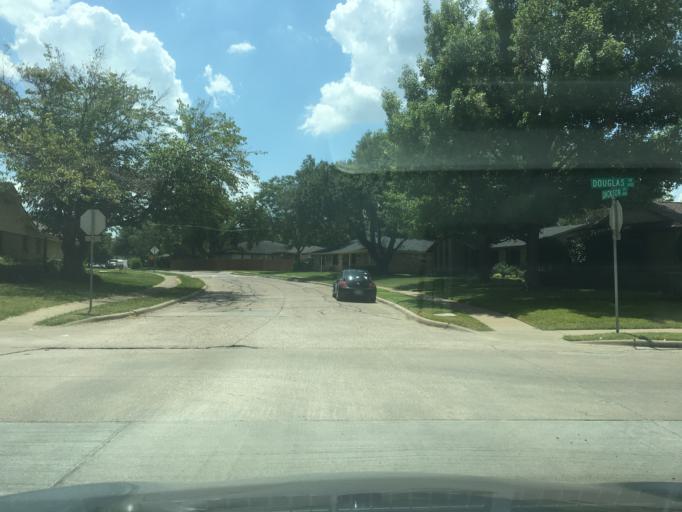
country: US
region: Texas
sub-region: Dallas County
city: Garland
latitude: 32.8686
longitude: -96.6523
